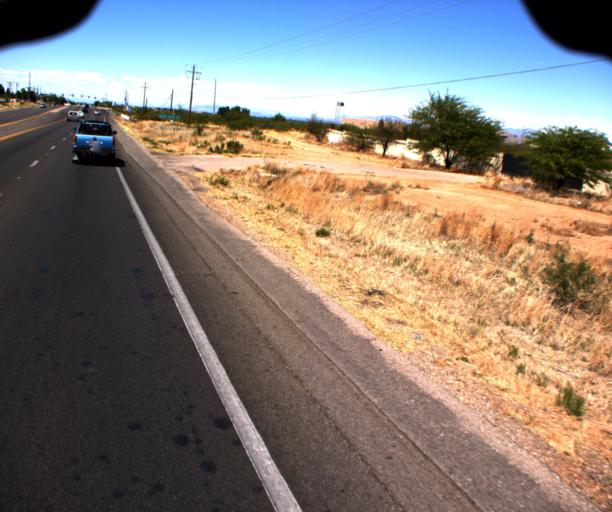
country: US
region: Arizona
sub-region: Cochise County
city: Sierra Vista
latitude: 31.5073
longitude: -110.2573
